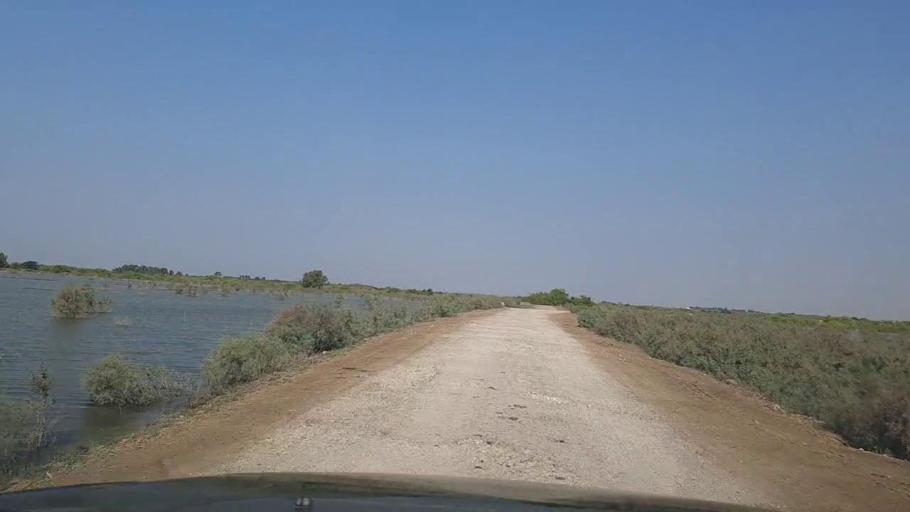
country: PK
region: Sindh
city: Thatta
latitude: 24.6395
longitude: 67.8143
